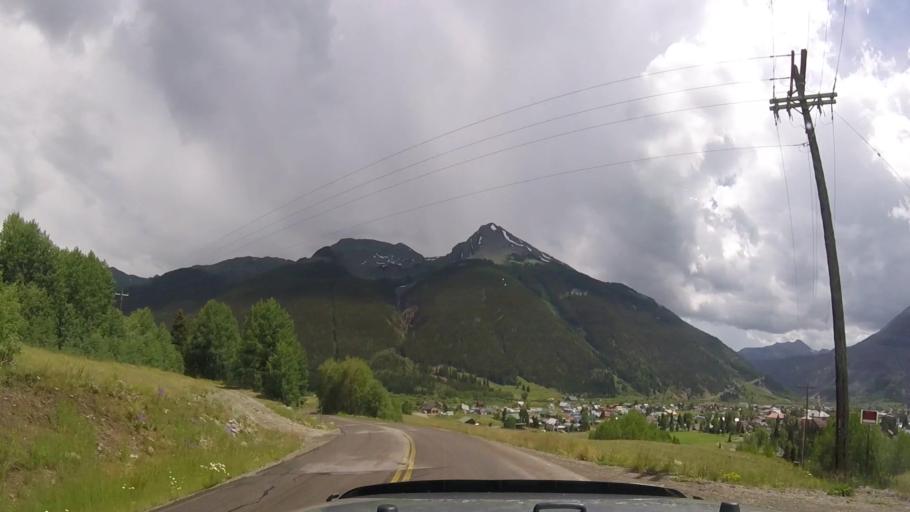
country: US
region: Colorado
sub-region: San Juan County
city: Silverton
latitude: 37.8197
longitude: -107.6606
